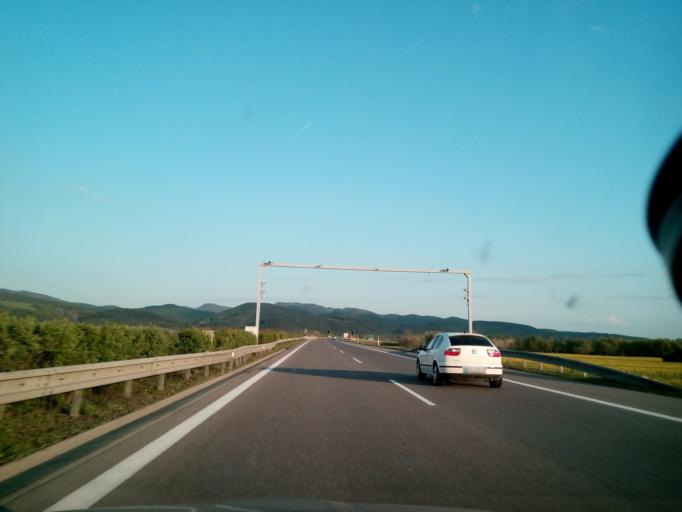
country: SK
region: Trenciansky
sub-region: Okres Nove Mesto nad Vahom
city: Nove Mesto nad Vahom
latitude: 48.7337
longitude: 17.8666
